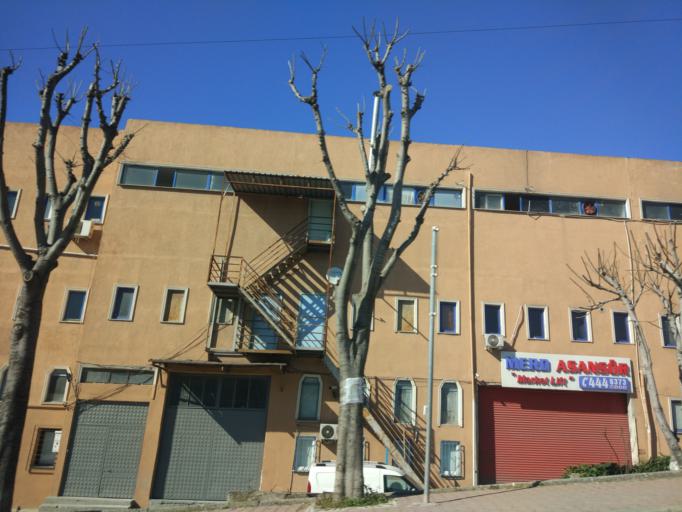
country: TR
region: Istanbul
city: Mahmutbey
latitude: 41.0151
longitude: 28.8154
